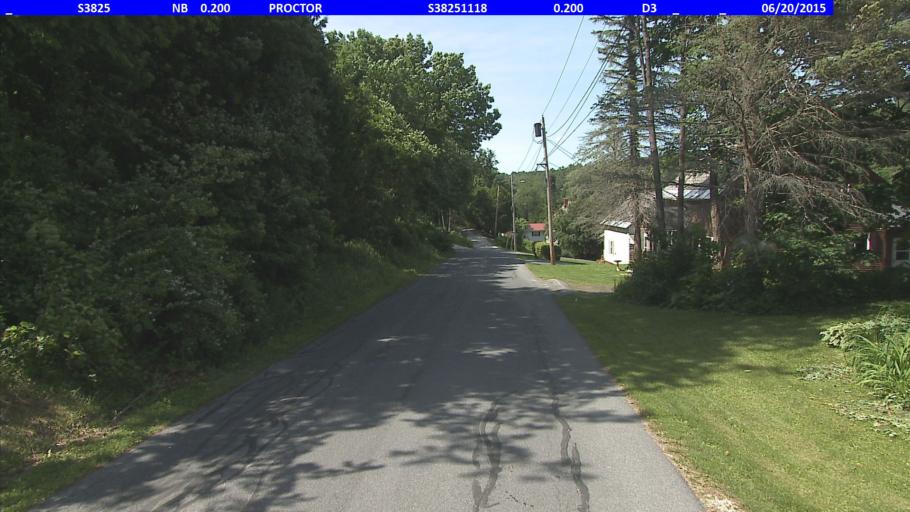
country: US
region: Vermont
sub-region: Rutland County
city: West Rutland
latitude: 43.6626
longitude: -73.0454
